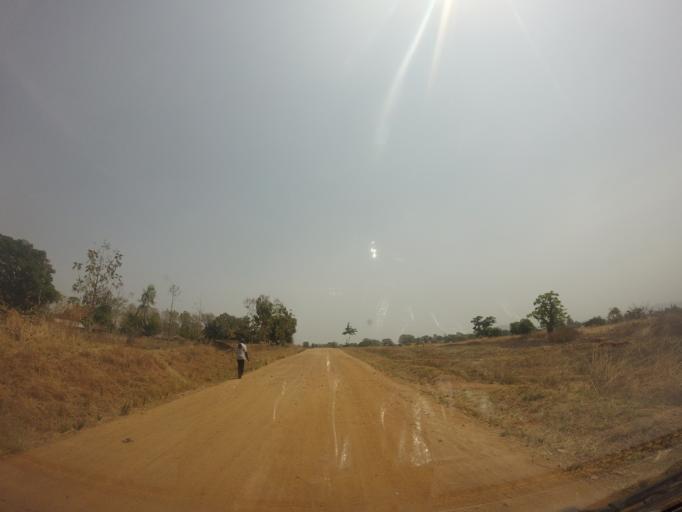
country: UG
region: Northern Region
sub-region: Arua District
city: Arua
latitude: 2.9151
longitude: 31.0213
